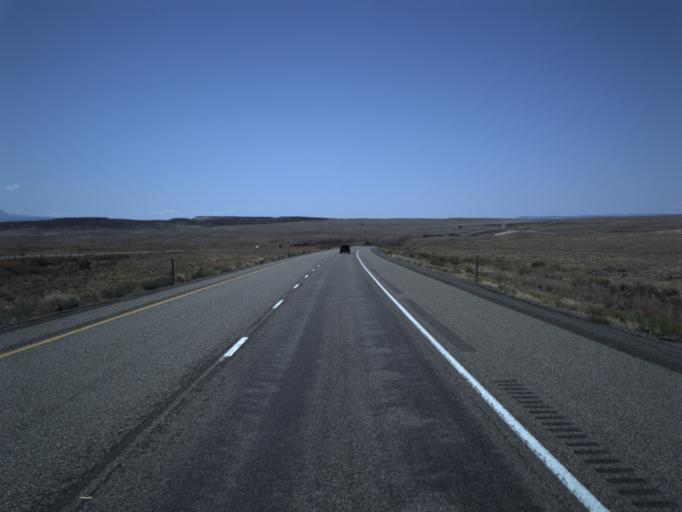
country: US
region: Colorado
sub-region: Mesa County
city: Loma
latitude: 39.1353
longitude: -109.1591
